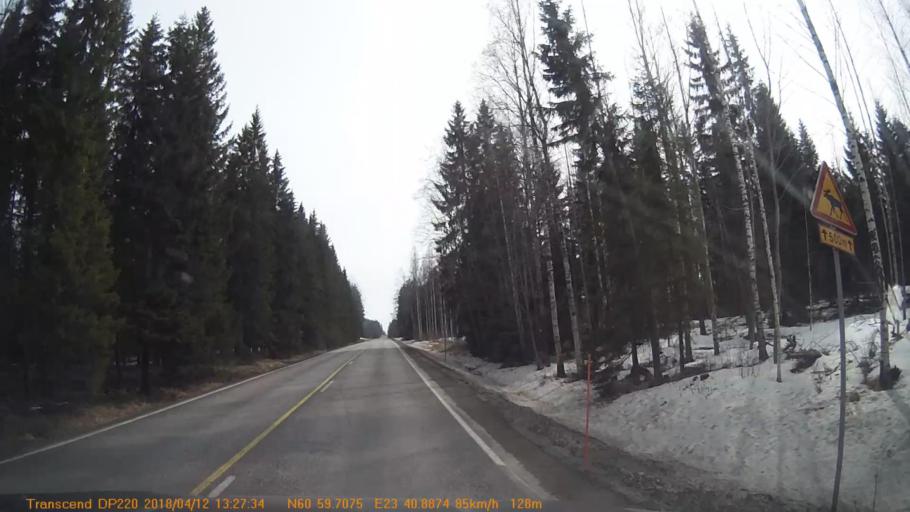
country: FI
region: Pirkanmaa
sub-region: Etelae-Pirkanmaa
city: Kylmaekoski
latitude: 60.9949
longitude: 23.6816
